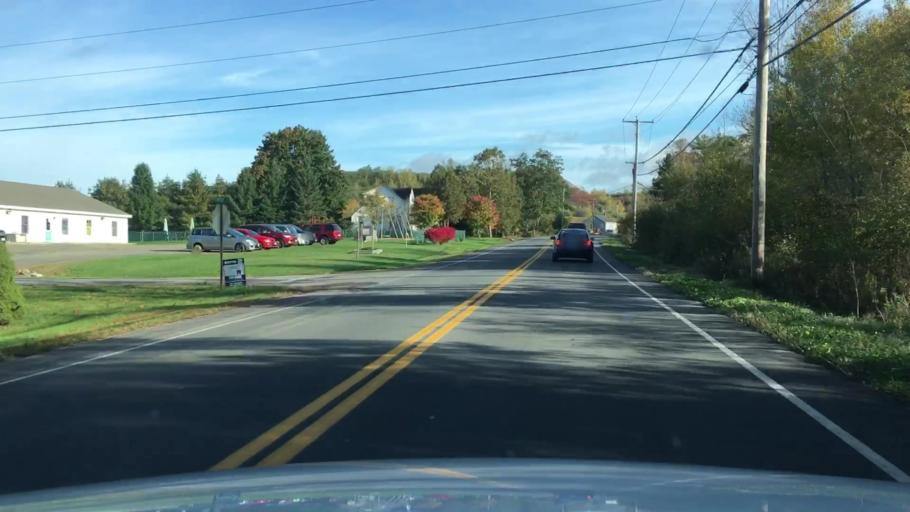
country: US
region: Maine
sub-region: Knox County
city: Thomaston
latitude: 44.0892
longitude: -69.1641
